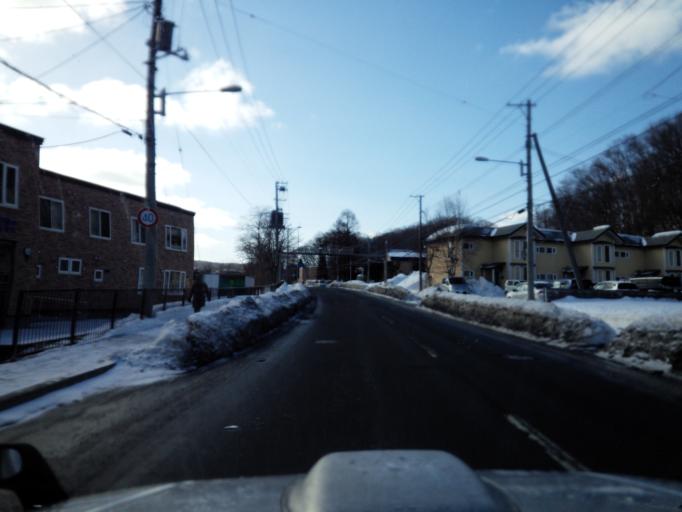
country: JP
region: Hokkaido
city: Sapporo
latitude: 42.9538
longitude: 141.3447
